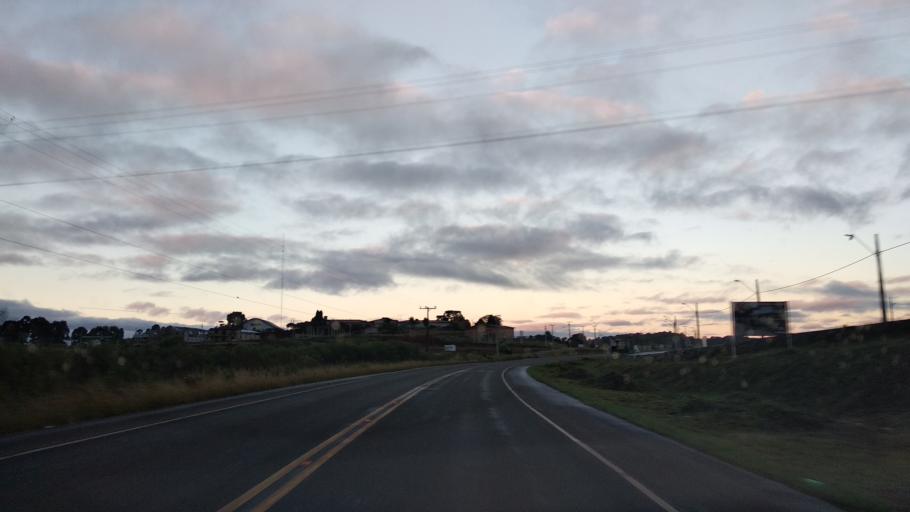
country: BR
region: Santa Catarina
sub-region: Campos Novos
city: Campos Novos
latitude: -27.3760
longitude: -51.2046
